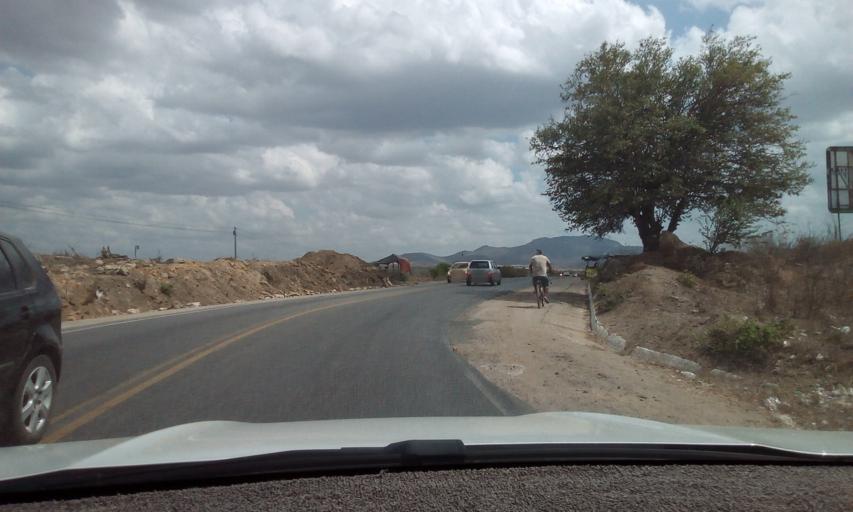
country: BR
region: Pernambuco
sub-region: Toritama
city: Toritama
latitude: -8.0187
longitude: -36.0527
